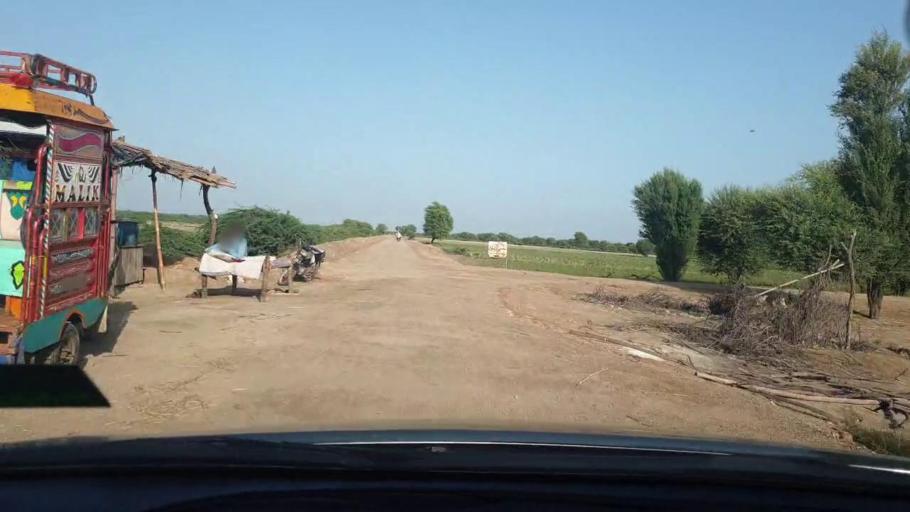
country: PK
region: Sindh
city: Naukot
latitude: 24.9032
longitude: 69.2821
